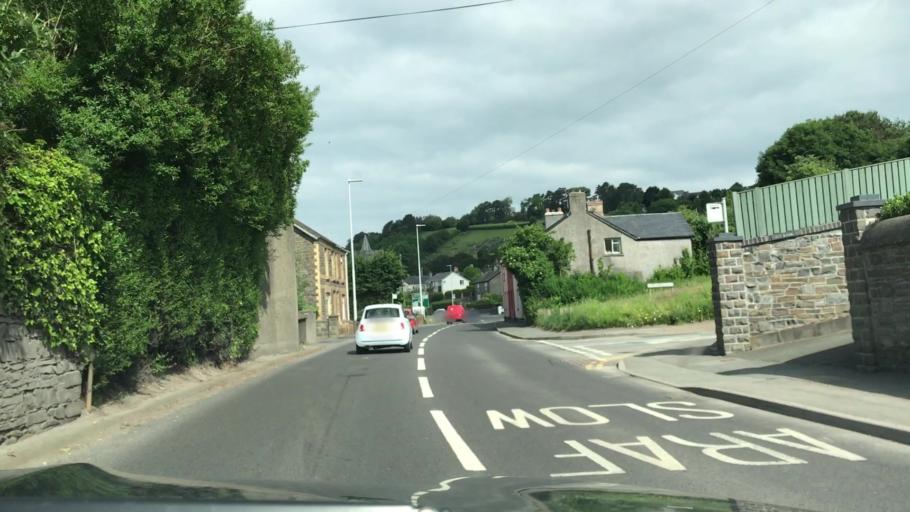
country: GB
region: Wales
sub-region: County of Ceredigion
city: Penparcau
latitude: 52.4061
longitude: -4.0568
